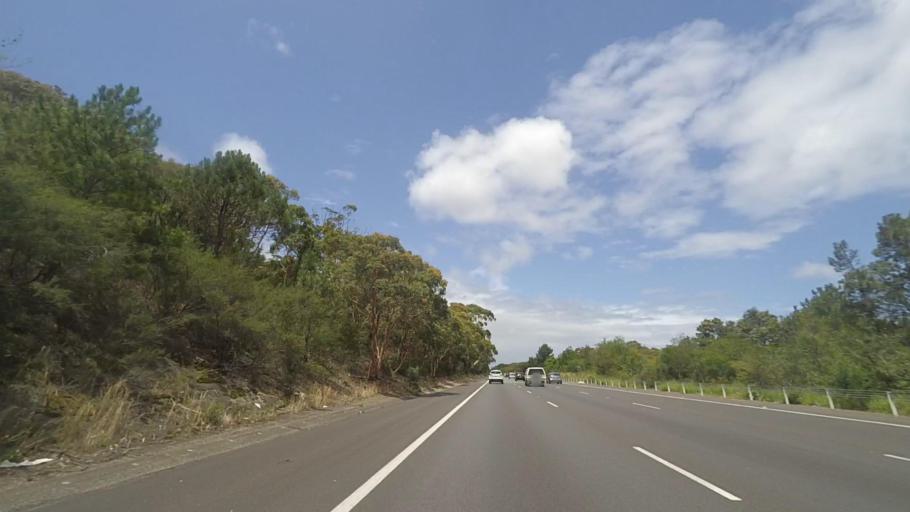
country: AU
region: New South Wales
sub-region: Gosford Shire
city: Narara
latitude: -33.3672
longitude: 151.3240
